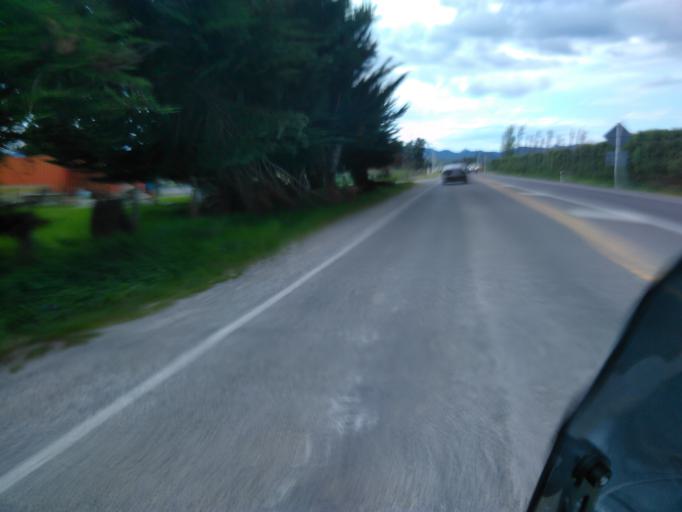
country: NZ
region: Gisborne
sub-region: Gisborne District
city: Gisborne
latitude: -38.6568
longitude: 177.9488
